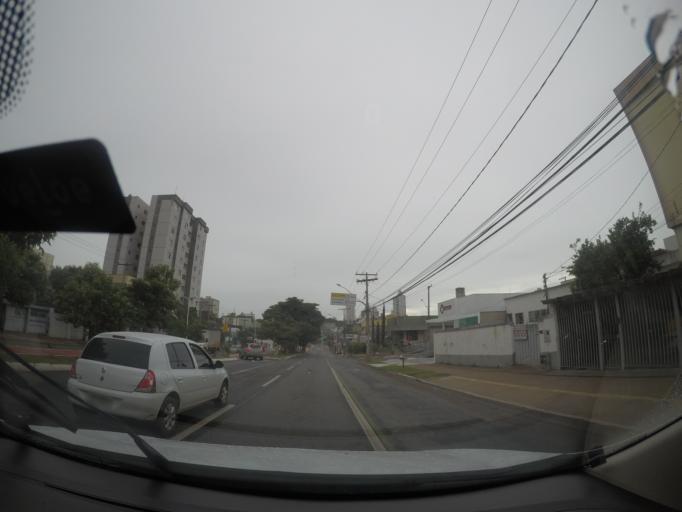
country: BR
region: Goias
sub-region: Goiania
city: Goiania
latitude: -16.6792
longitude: -49.2512
